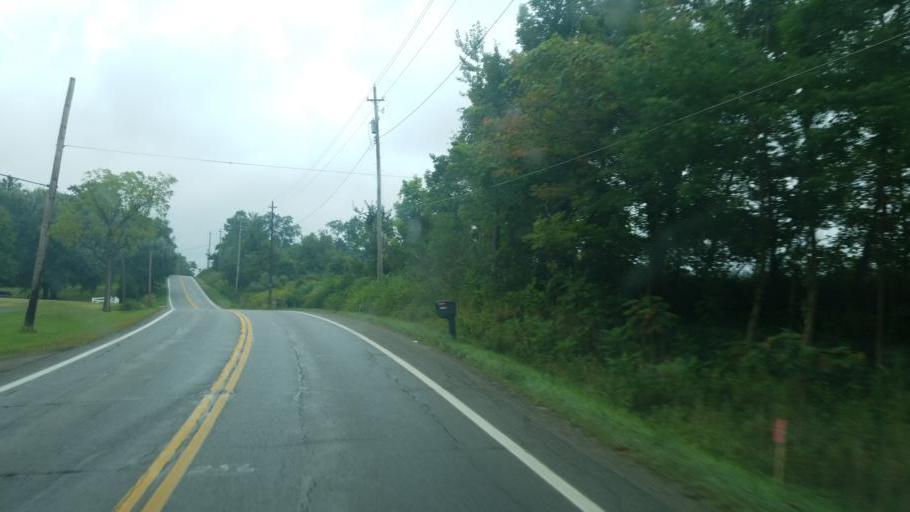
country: US
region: Ohio
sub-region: Geauga County
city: Burton
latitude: 41.4534
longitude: -81.1988
